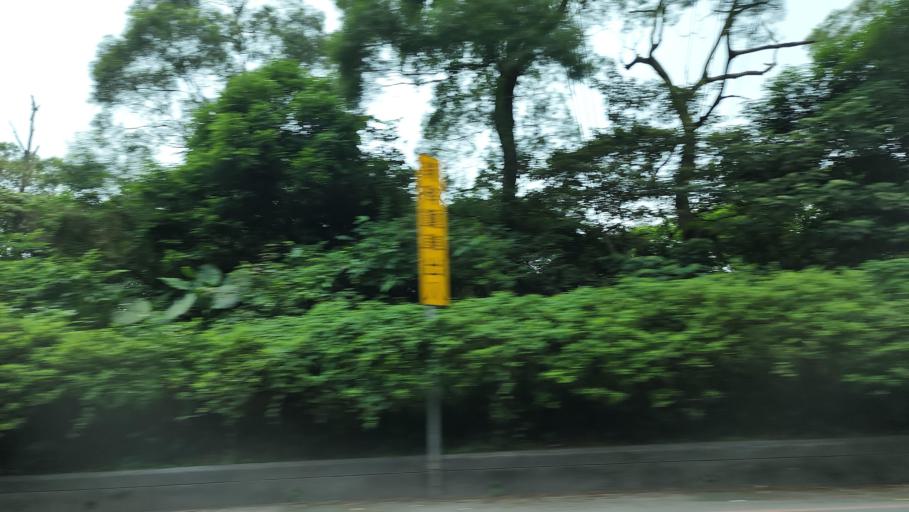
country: TW
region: Taiwan
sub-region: Keelung
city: Keelung
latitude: 25.1640
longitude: 121.6869
